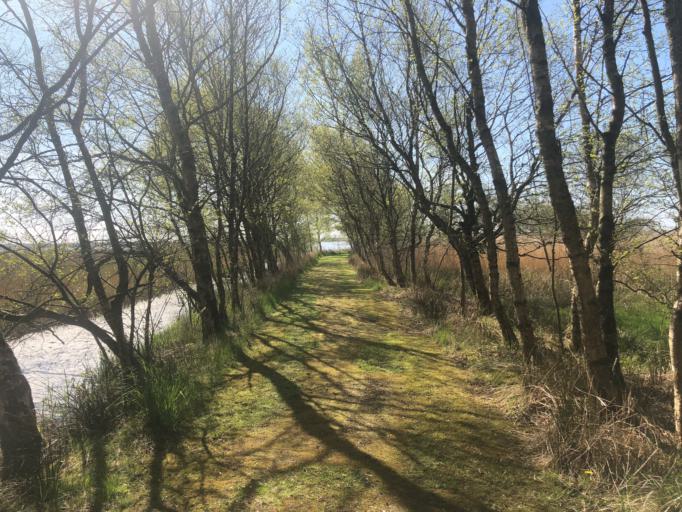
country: DK
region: Central Jutland
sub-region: Holstebro Kommune
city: Vinderup
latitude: 56.5698
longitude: 8.7912
